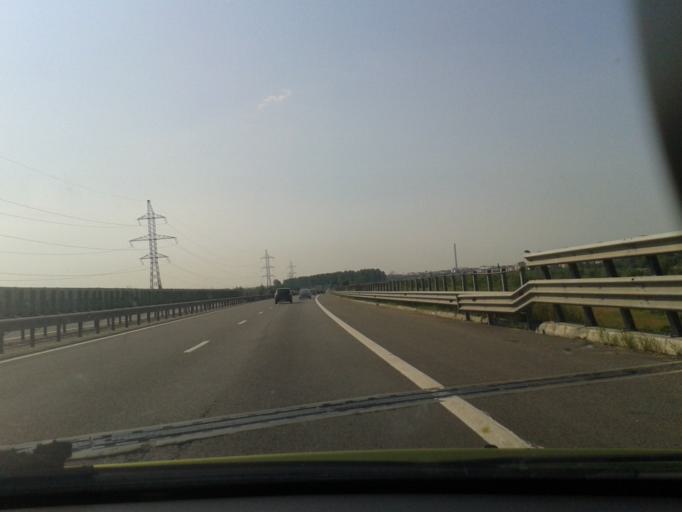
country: RO
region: Arges
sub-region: Comuna Albestii de Arges
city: Pitesti
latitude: 44.8630
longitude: 24.8877
